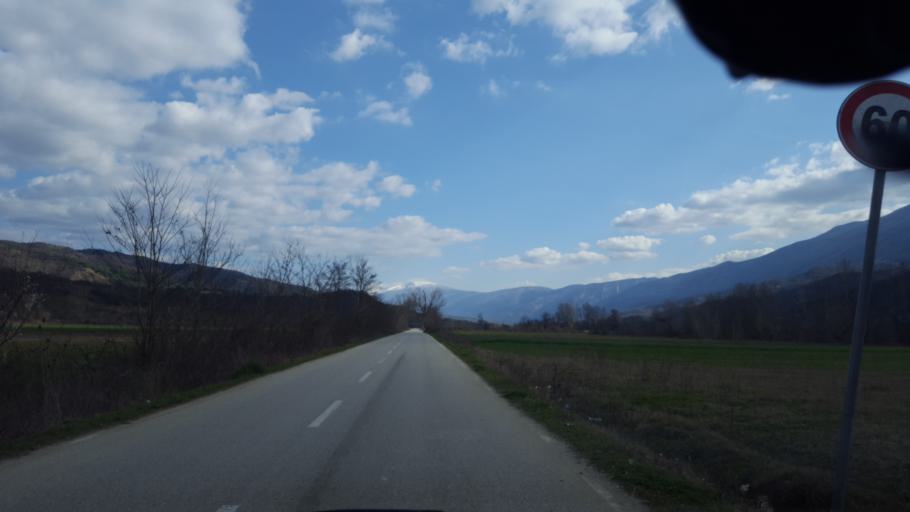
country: AL
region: Gjirokaster
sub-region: Rrethi i Permetit
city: Ballaban
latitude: 40.4133
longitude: 20.1247
